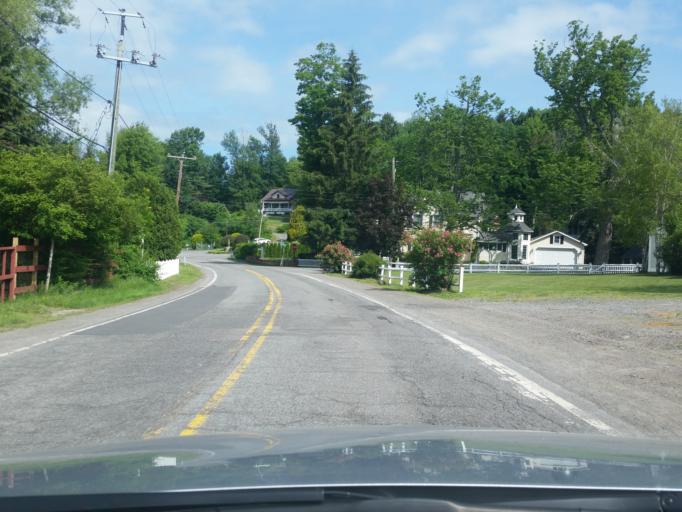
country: US
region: Pennsylvania
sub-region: Luzerne County
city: Harveys Lake
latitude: 41.3601
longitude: -76.0320
